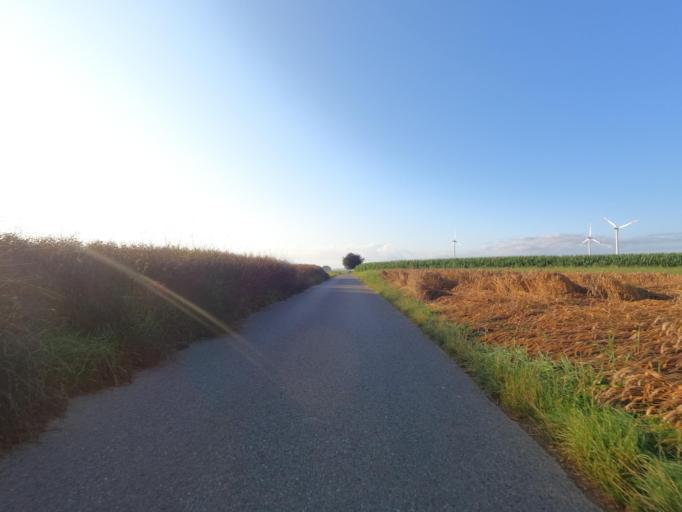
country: DE
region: North Rhine-Westphalia
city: Erkelenz
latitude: 51.0255
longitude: 6.3490
